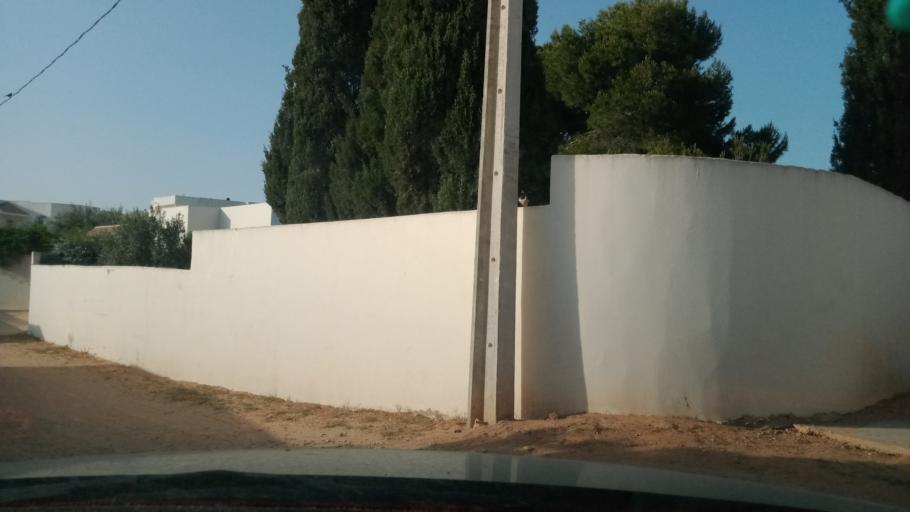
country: TN
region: Safaqis
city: Al Qarmadah
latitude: 34.8201
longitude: 10.7457
